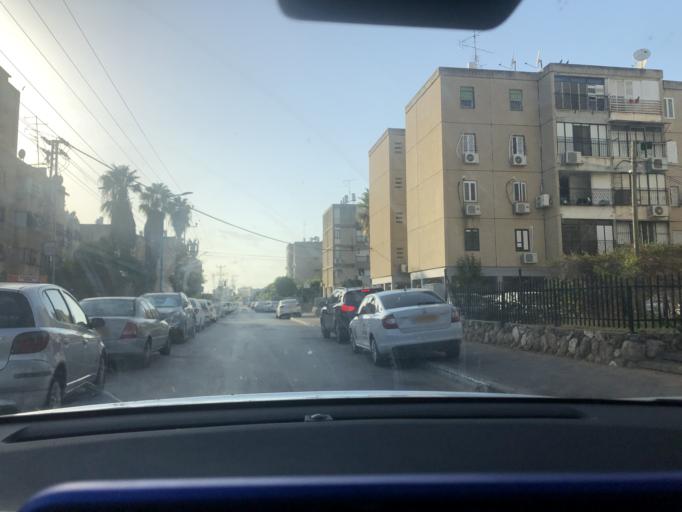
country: IL
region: Central District
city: Lod
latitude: 31.9509
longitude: 34.8884
